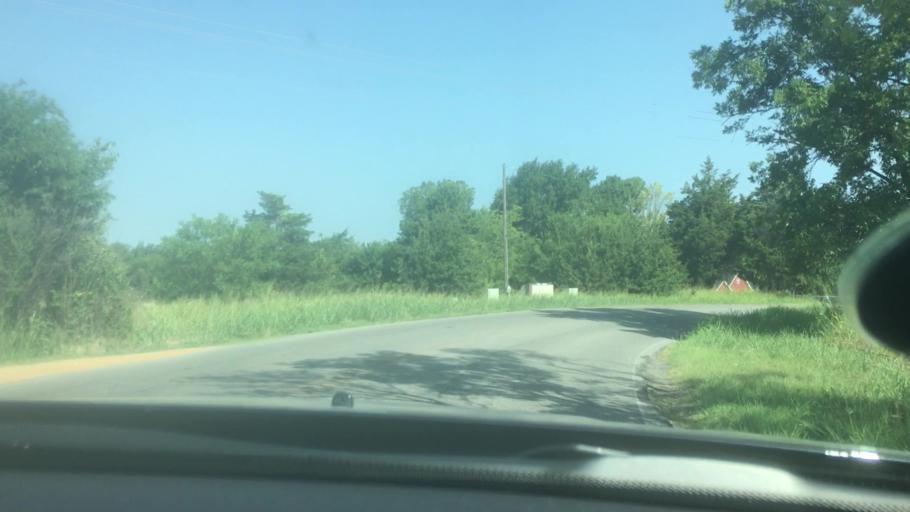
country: US
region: Oklahoma
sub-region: Bryan County
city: Calera
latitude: 34.0200
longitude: -96.4739
